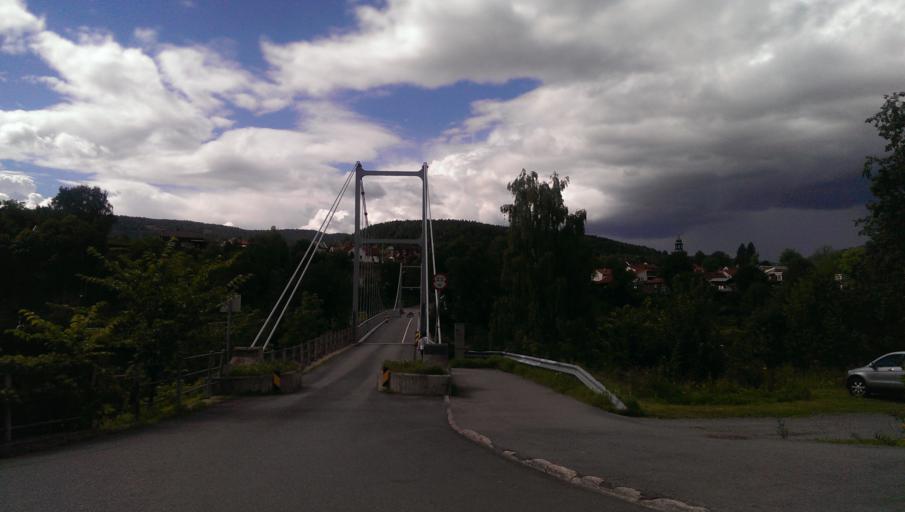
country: NO
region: Buskerud
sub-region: Kongsberg
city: Kongsberg
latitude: 59.6623
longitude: 9.6543
